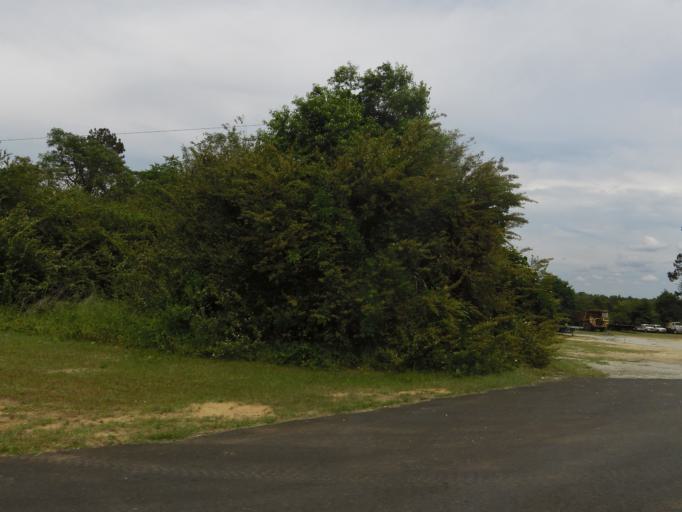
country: US
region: Georgia
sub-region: McDuffie County
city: Thomson
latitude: 33.3606
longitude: -82.4645
